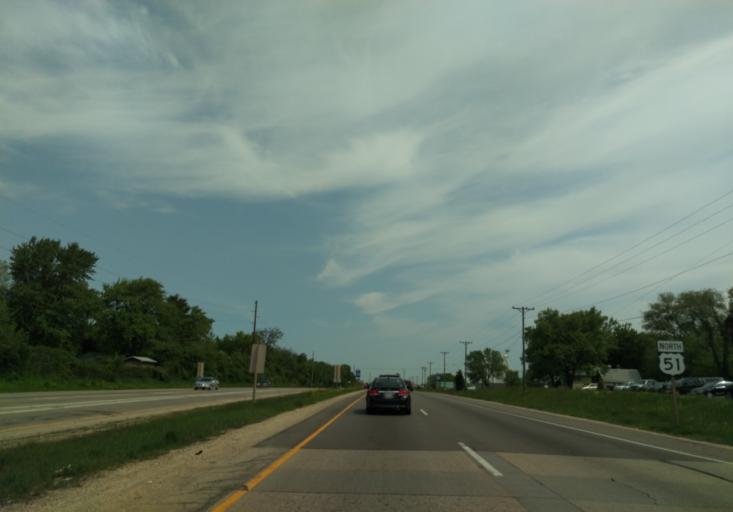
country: US
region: Wisconsin
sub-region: Dane County
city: Monona
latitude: 43.0740
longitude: -89.3098
